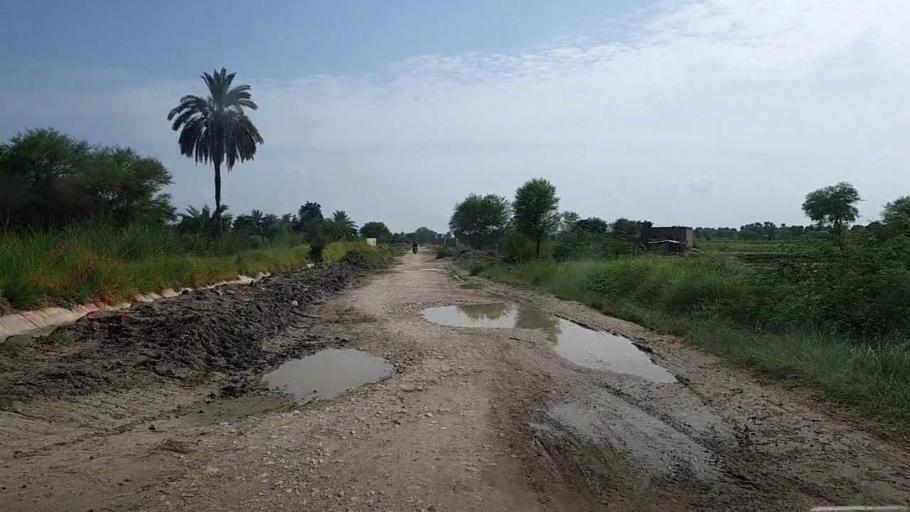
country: PK
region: Sindh
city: Bhiria
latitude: 26.8819
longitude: 68.2333
